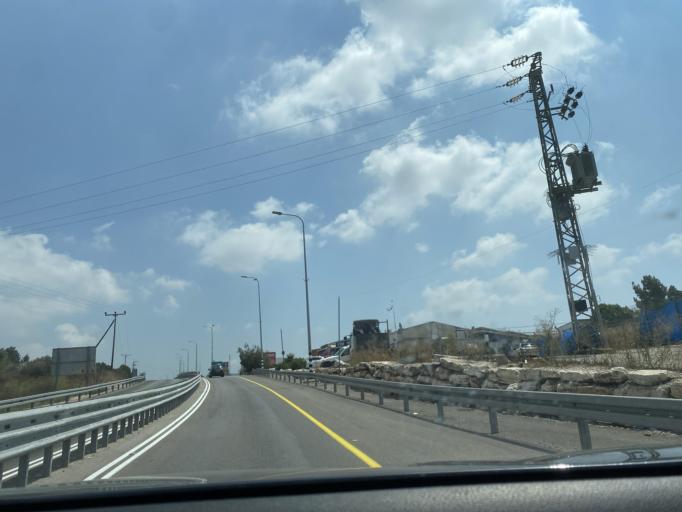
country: IL
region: Northern District
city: Kefar Weradim
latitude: 33.0026
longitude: 35.2974
